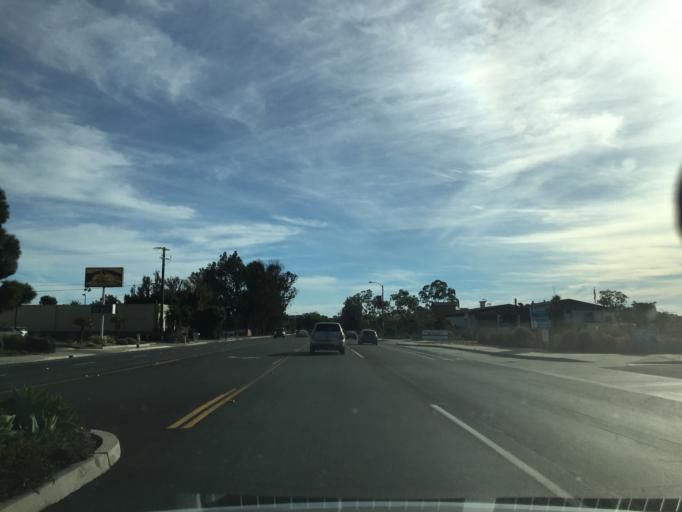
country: US
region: California
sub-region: Santa Barbara County
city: Isla Vista
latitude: 34.4270
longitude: -119.8698
